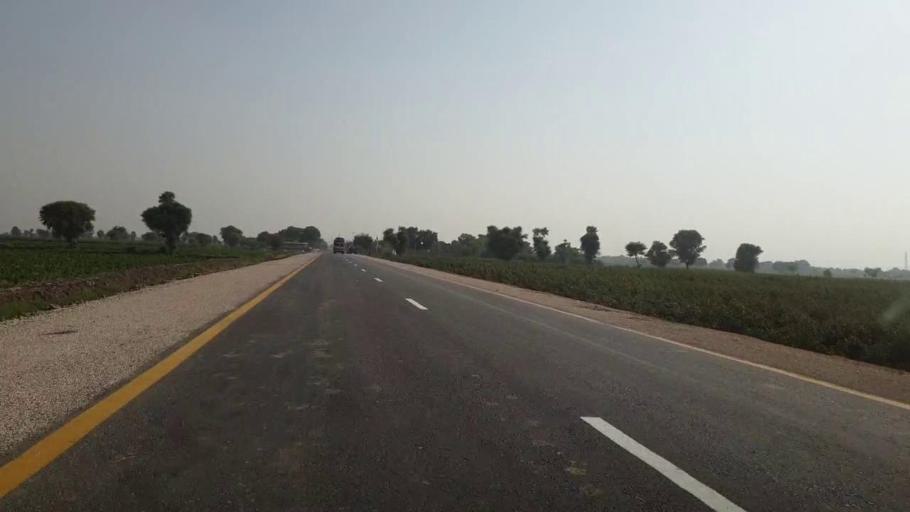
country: PK
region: Sindh
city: Bhan
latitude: 26.5386
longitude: 67.7879
